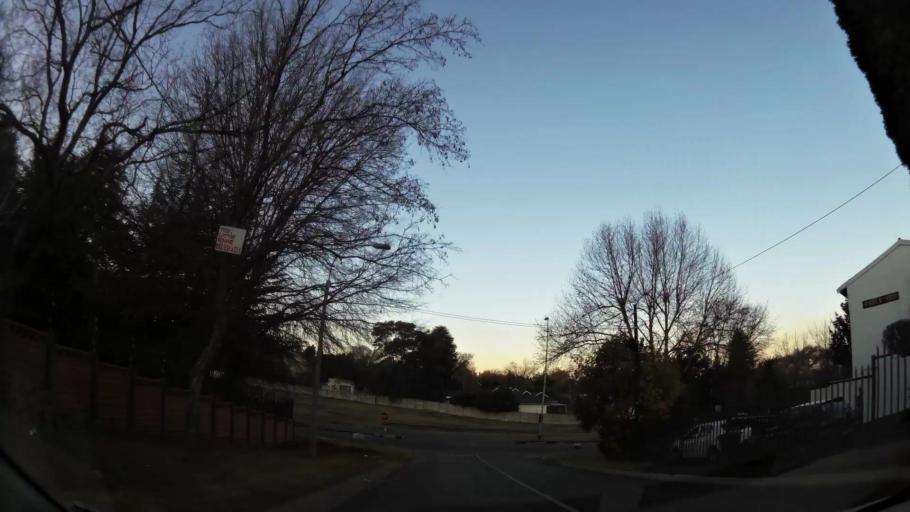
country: ZA
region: Gauteng
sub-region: City of Johannesburg Metropolitan Municipality
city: Roodepoort
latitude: -26.1572
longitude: 27.9051
